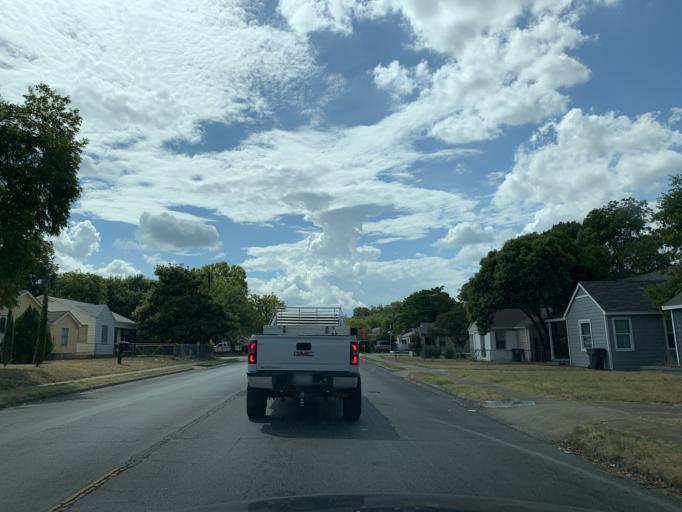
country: US
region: Texas
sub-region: Dallas County
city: Cockrell Hill
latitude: 32.7350
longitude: -96.8629
